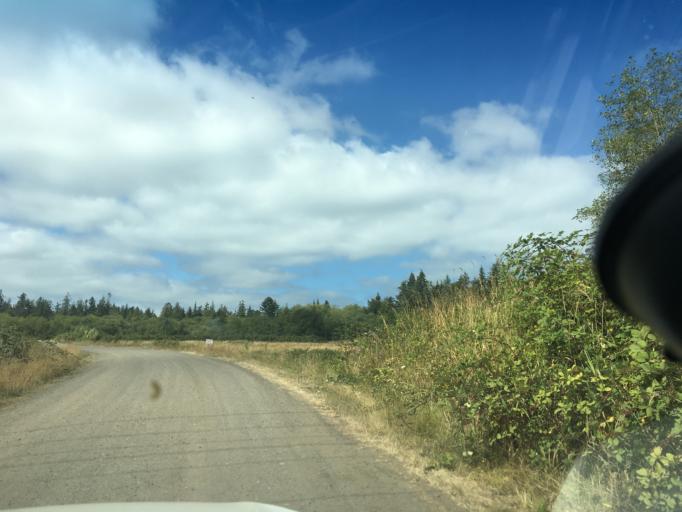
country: US
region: Washington
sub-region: Kitsap County
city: Hansville
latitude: 47.8478
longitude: -122.5856
